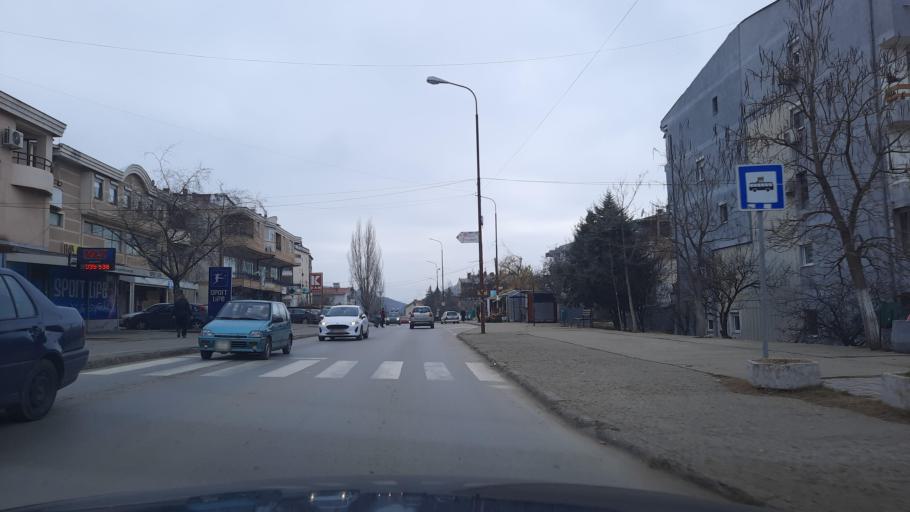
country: MK
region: Stip
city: Shtip
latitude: 41.7498
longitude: 22.1999
